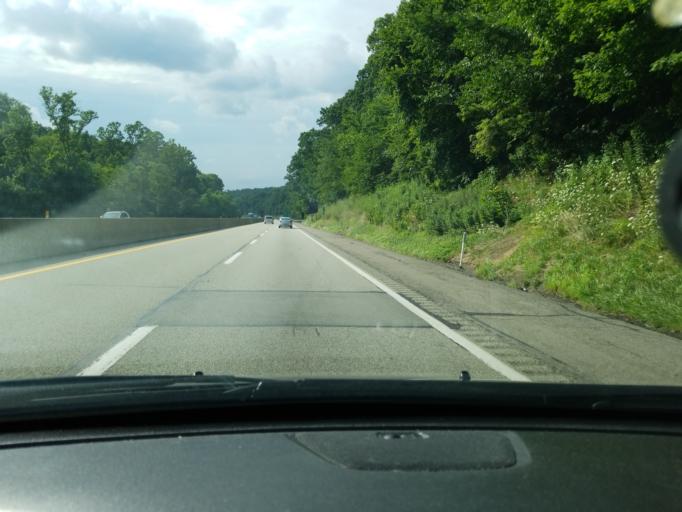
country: US
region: Pennsylvania
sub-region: Beaver County
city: West Mayfield
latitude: 40.8015
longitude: -80.2972
